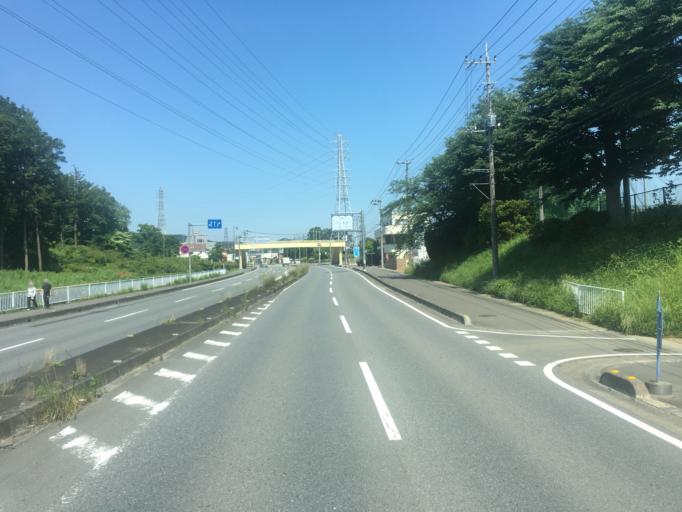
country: JP
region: Saitama
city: Ogawa
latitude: 36.0376
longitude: 139.3246
